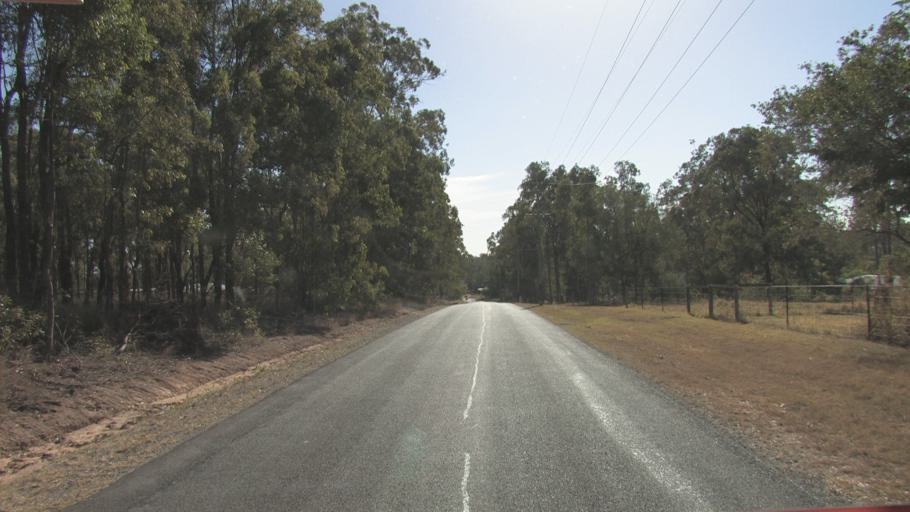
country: AU
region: Queensland
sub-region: Logan
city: Cedar Vale
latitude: -27.8542
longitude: 152.9933
